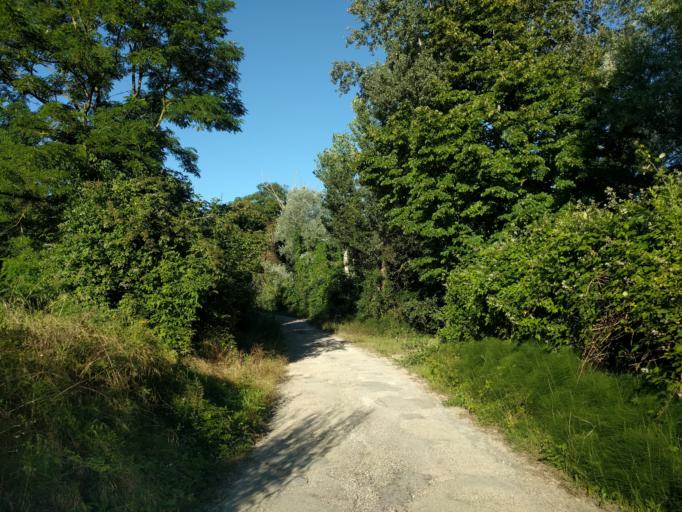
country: IT
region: The Marches
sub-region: Provincia di Pesaro e Urbino
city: Cuccurano
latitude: 43.8164
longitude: 12.9329
